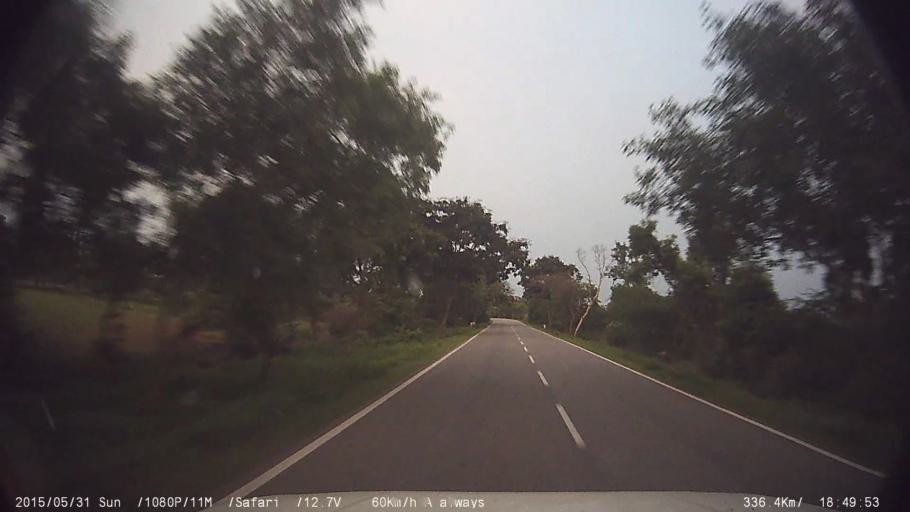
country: IN
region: Karnataka
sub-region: Mysore
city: Tirumakudal Narsipur
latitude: 12.1758
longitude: 76.8540
